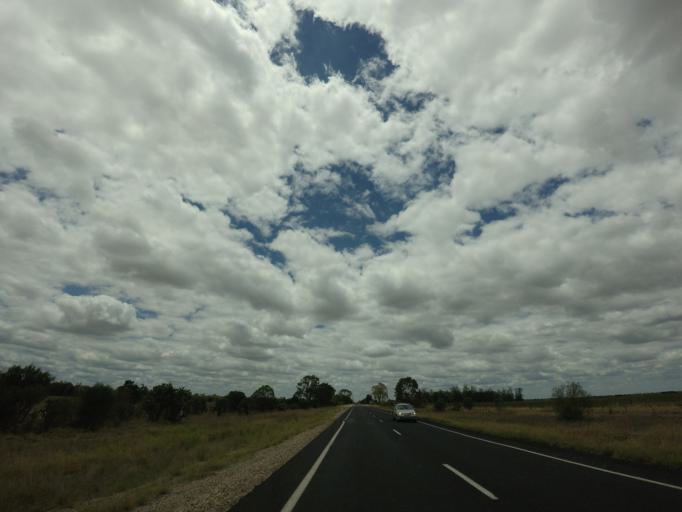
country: AU
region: Queensland
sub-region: Goondiwindi
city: Goondiwindi
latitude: -28.1757
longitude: 150.4822
